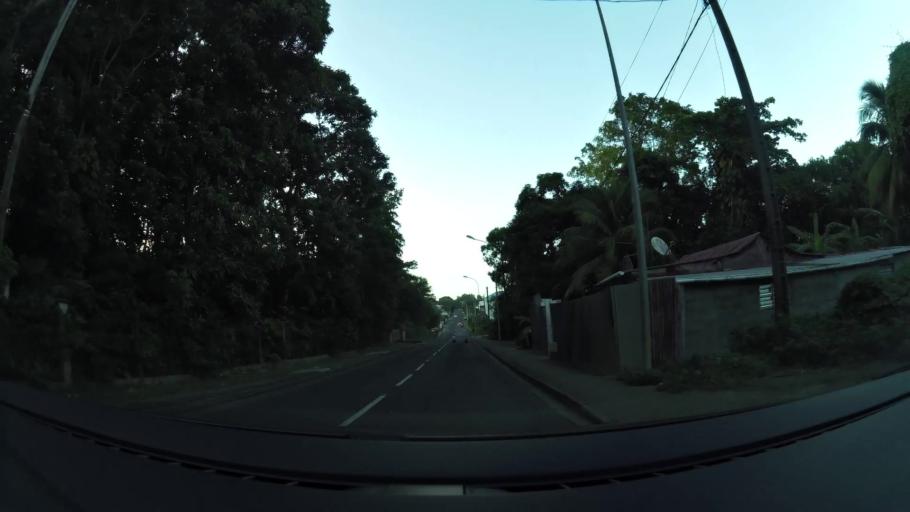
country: GP
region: Guadeloupe
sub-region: Guadeloupe
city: Les Abymes
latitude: 16.2622
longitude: -61.5062
